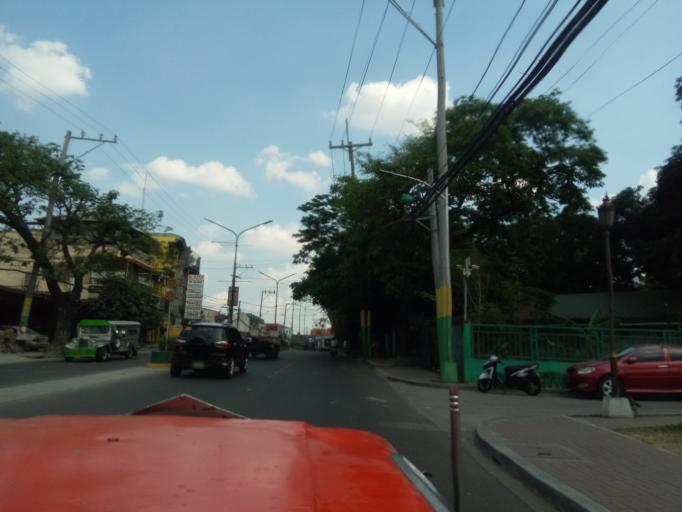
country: PH
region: Calabarzon
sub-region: Province of Cavite
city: Dasmarinas
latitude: 14.3244
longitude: 120.9624
